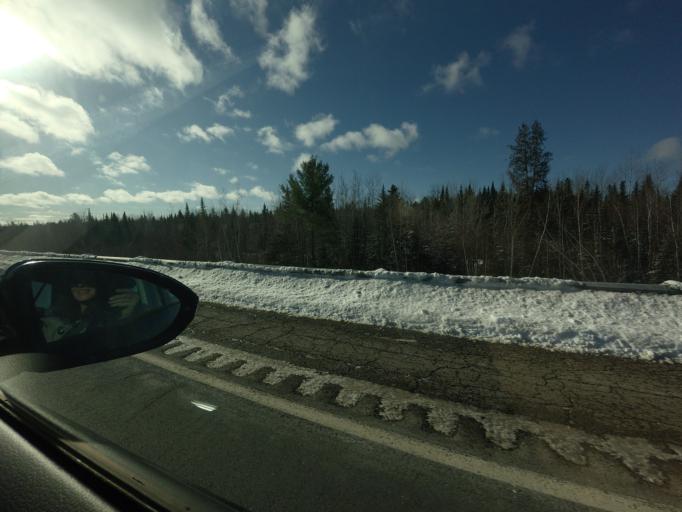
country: CA
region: New Brunswick
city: Fredericton
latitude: 45.8822
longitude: -66.6381
